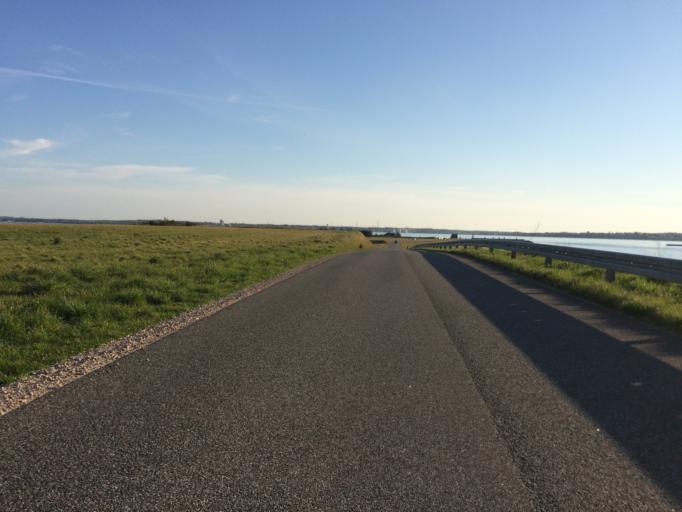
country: DK
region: Central Jutland
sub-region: Struer Kommune
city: Struer
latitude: 56.5195
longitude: 8.6254
